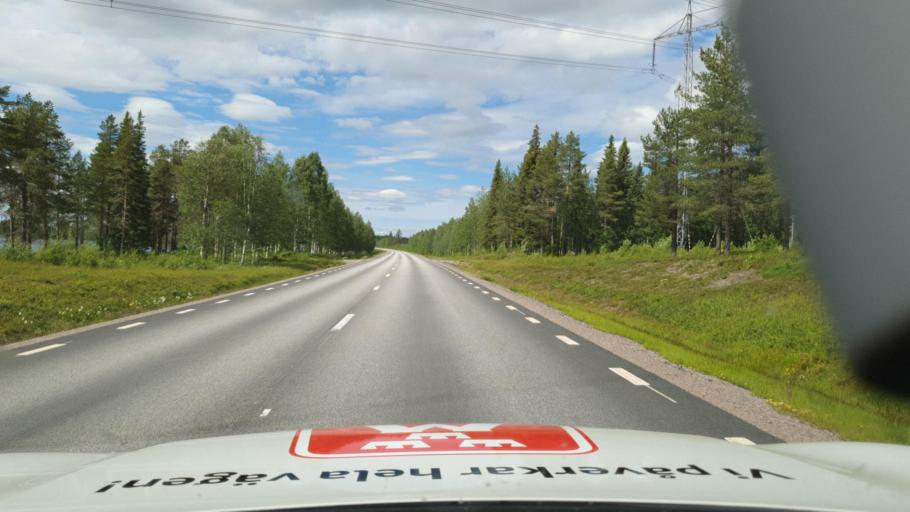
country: SE
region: Vaesterbotten
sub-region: Norsjo Kommun
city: Norsjoe
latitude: 65.1927
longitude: 19.8379
